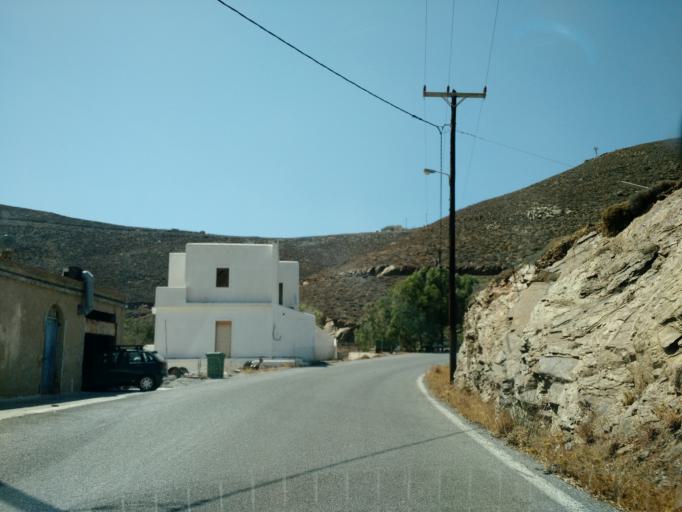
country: GR
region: South Aegean
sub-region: Nomos Dodekanisou
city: Astypalaia
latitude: 36.5506
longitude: 26.3517
